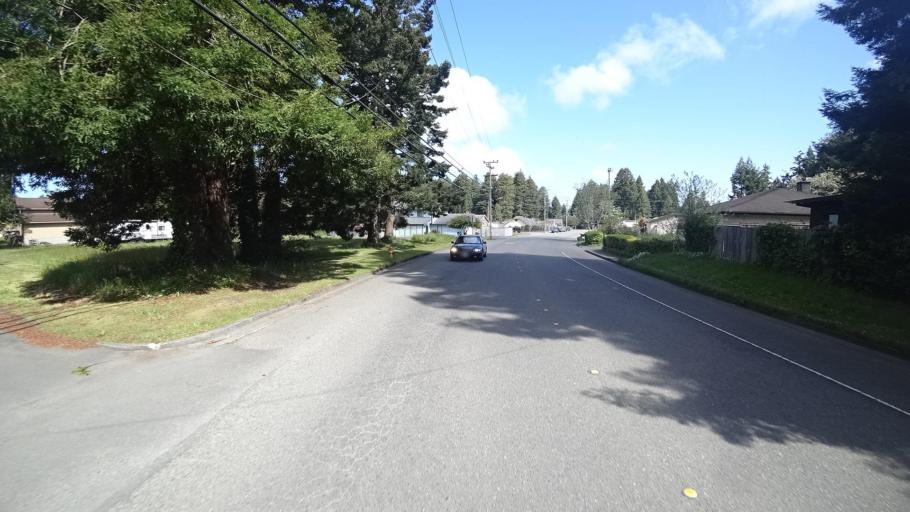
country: US
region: California
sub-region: Humboldt County
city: Cutten
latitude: 40.7597
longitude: -124.1542
